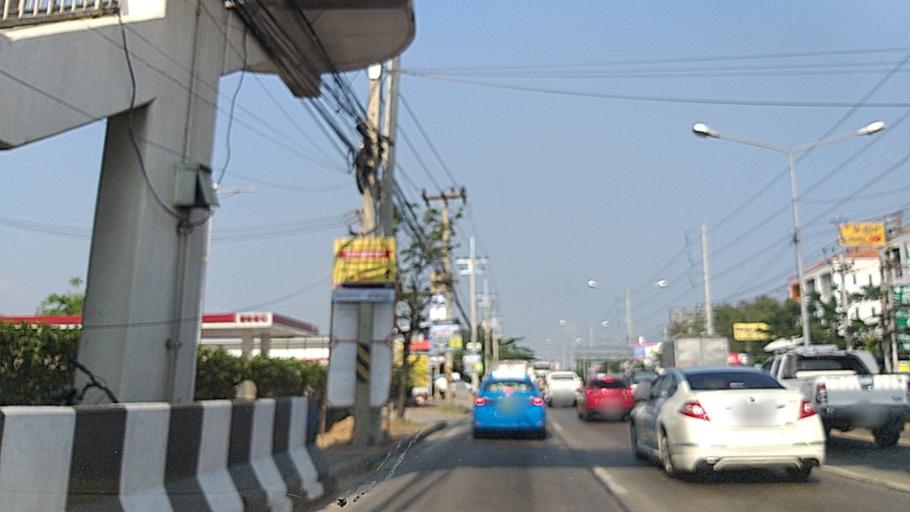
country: TH
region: Bangkok
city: Sai Mai
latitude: 13.9331
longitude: 100.6965
